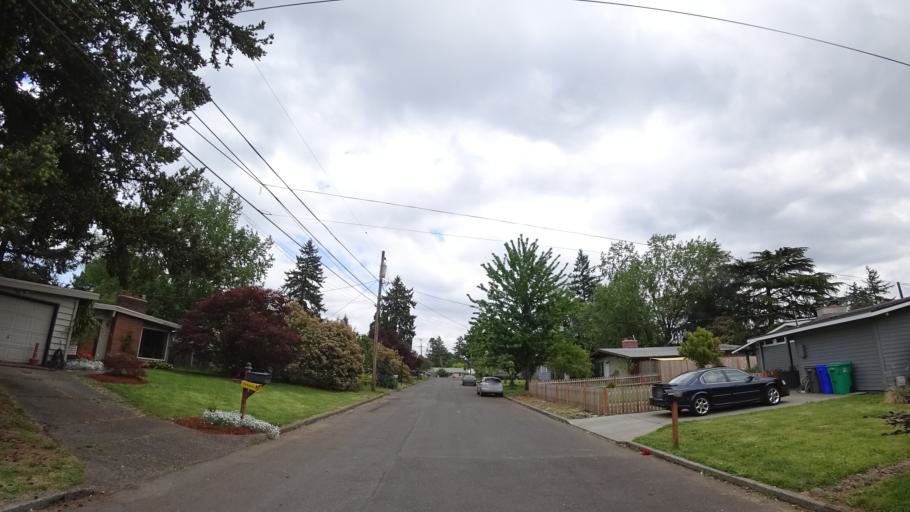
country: US
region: Oregon
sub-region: Multnomah County
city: Lents
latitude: 45.5073
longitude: -122.5441
